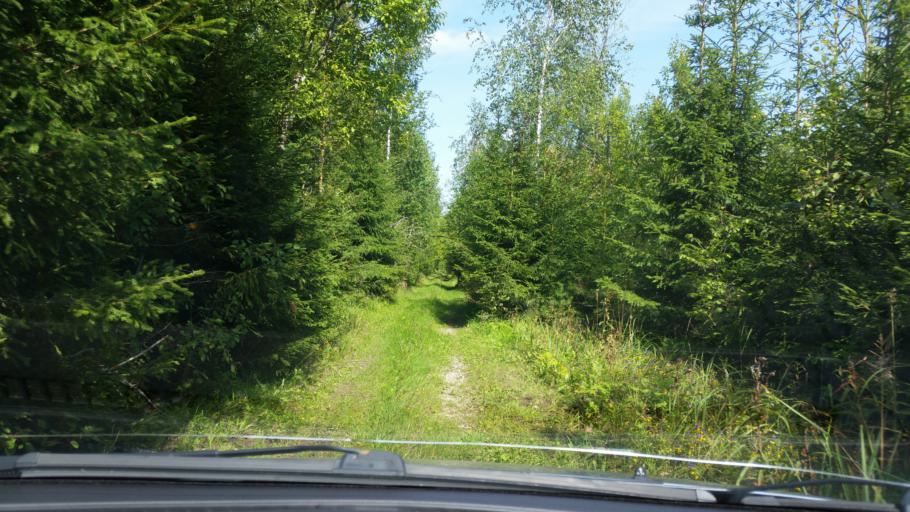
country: RU
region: Moskovskaya
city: Bol'shoye Gryzlovo
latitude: 54.9107
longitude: 37.7549
